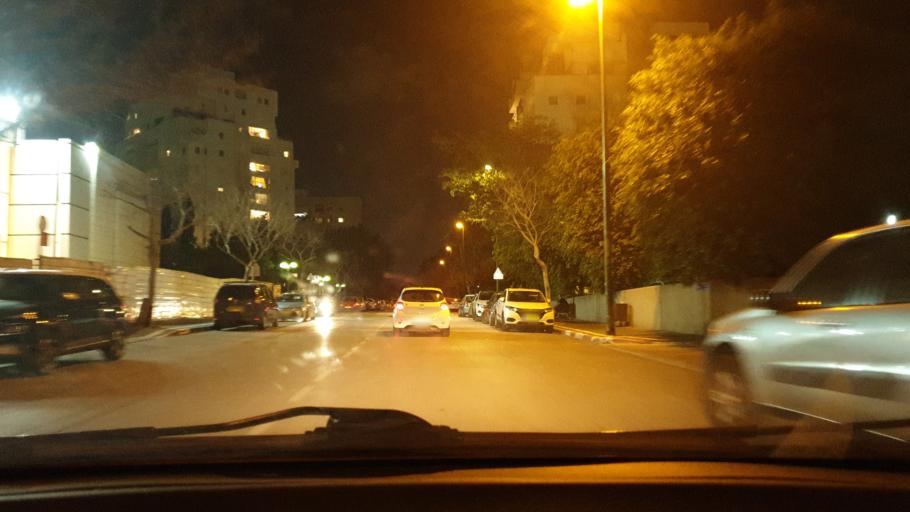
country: IL
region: Tel Aviv
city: Ramat HaSharon
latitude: 32.1255
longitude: 34.8010
